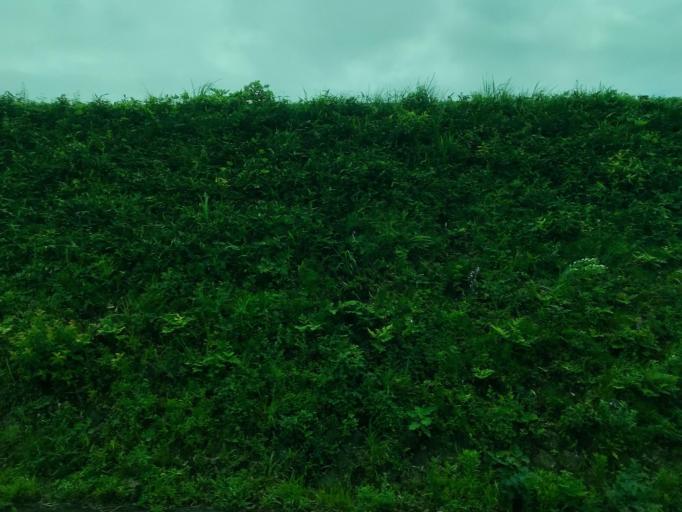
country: JP
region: Tochigi
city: Kuroiso
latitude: 37.0091
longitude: 140.0947
